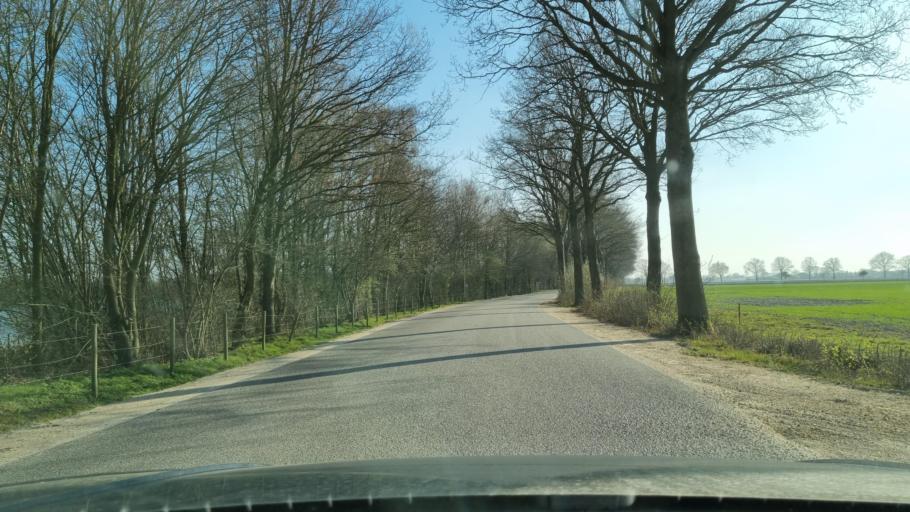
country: NL
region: Limburg
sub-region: Gemeente Gennep
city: Gennep
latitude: 51.7285
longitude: 5.9994
